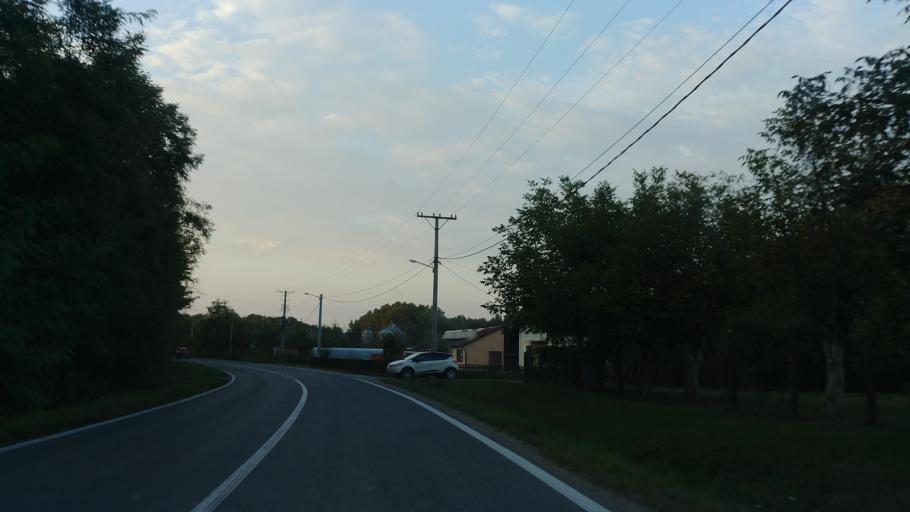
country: BA
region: Brcko
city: Brcko
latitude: 44.7939
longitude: 18.8161
